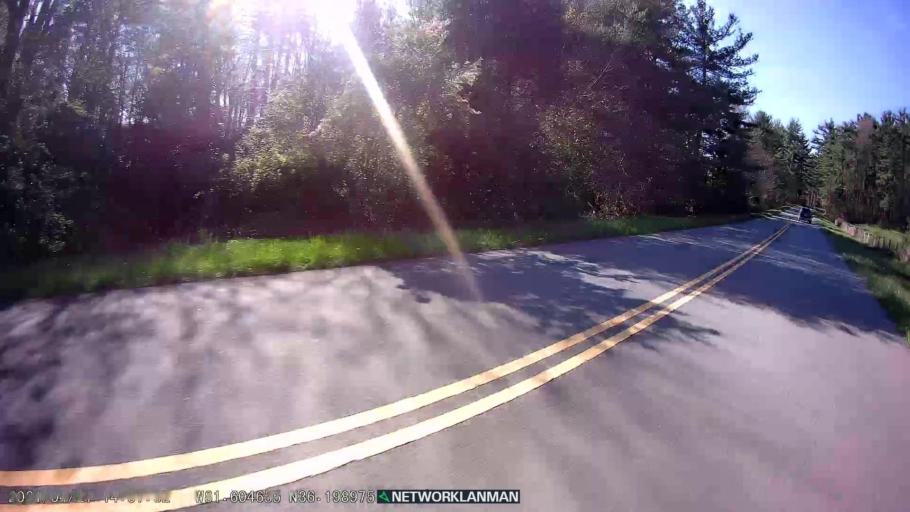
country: US
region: North Carolina
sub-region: Watauga County
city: Boone
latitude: 36.1992
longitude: -81.6048
